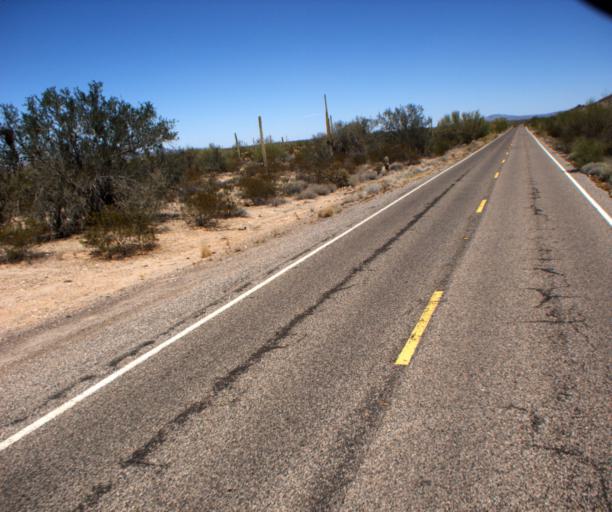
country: US
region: Arizona
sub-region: Pima County
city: Ajo
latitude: 32.2056
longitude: -112.7588
